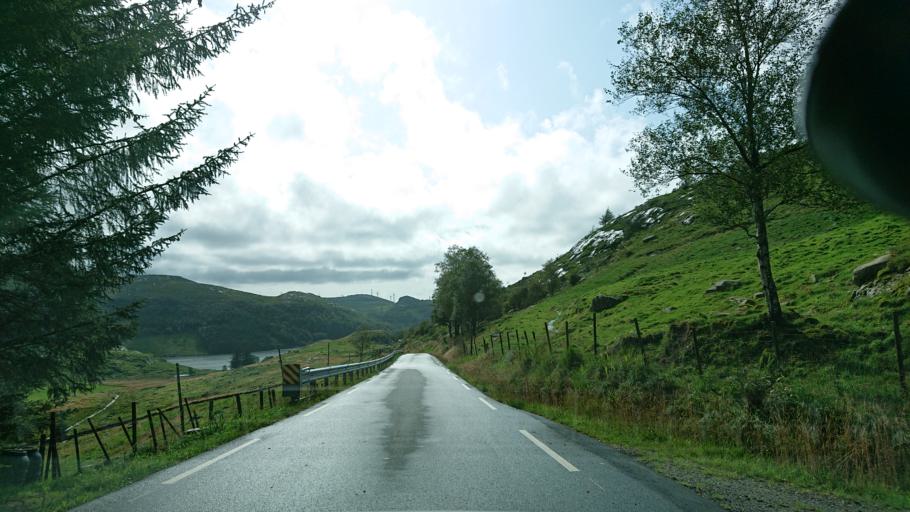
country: NO
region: Rogaland
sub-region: Gjesdal
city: Algard
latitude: 58.6797
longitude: 5.8505
